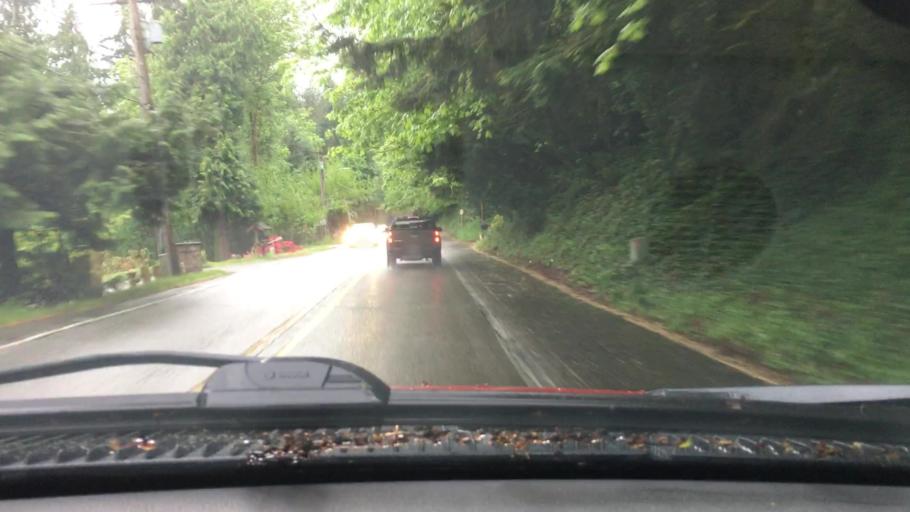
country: US
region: Washington
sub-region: King County
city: West Lake Sammamish
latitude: 47.5947
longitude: -122.1115
